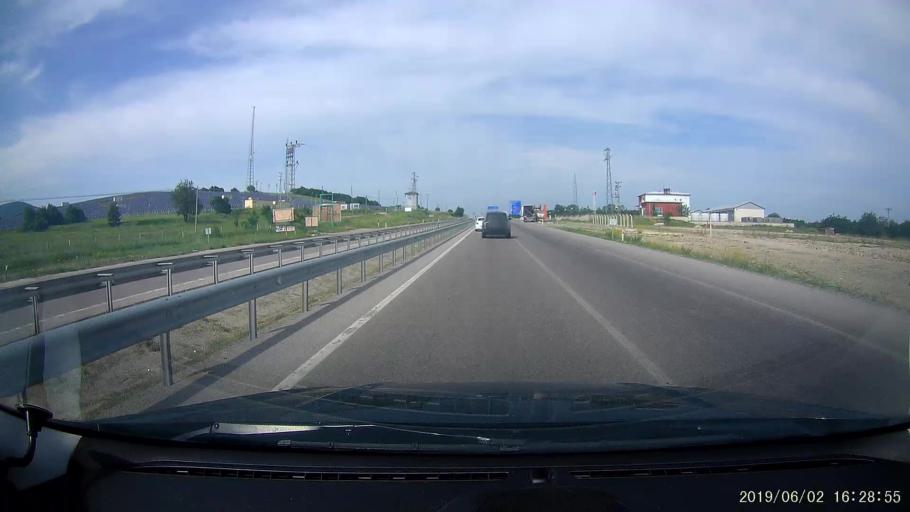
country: TR
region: Samsun
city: Ladik
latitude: 41.0095
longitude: 35.8587
